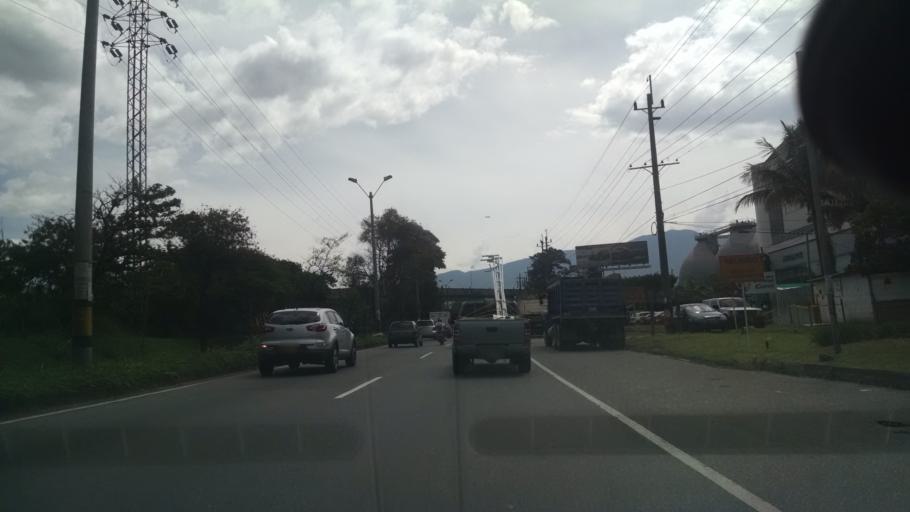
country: CO
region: Antioquia
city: Envigado
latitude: 6.1878
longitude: -75.5847
